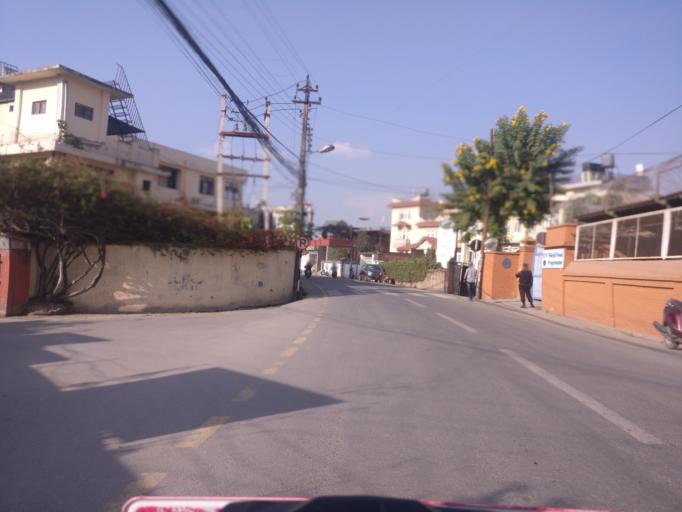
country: NP
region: Central Region
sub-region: Bagmati Zone
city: Patan
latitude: 27.6803
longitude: 85.3205
